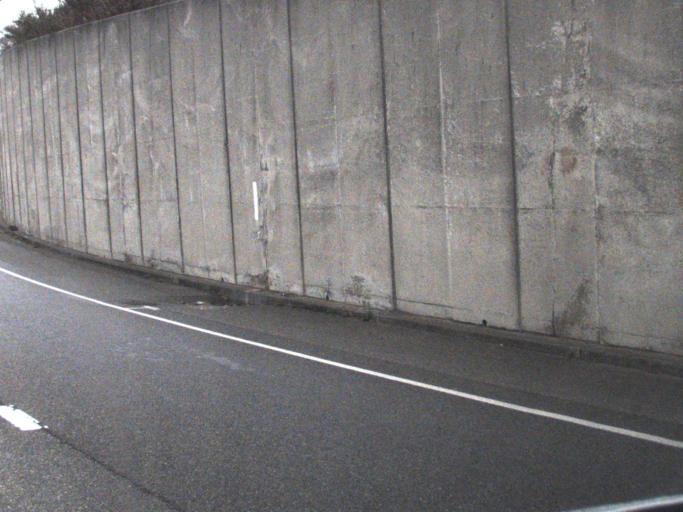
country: US
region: Washington
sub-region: Snohomish County
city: Mukilteo
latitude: 47.9221
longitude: -122.2781
